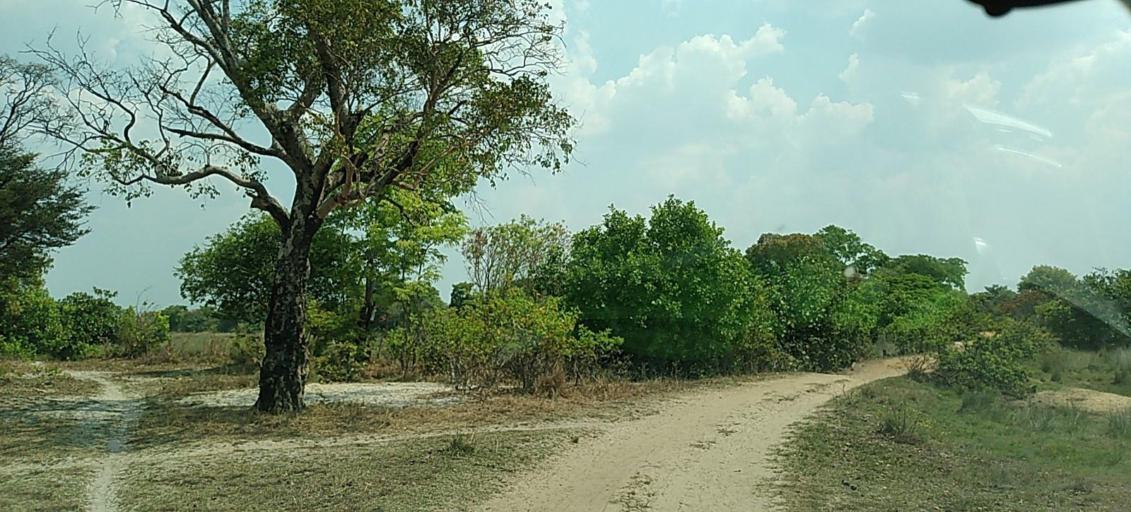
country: ZM
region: North-Western
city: Kabompo
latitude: -13.3565
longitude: 23.8945
